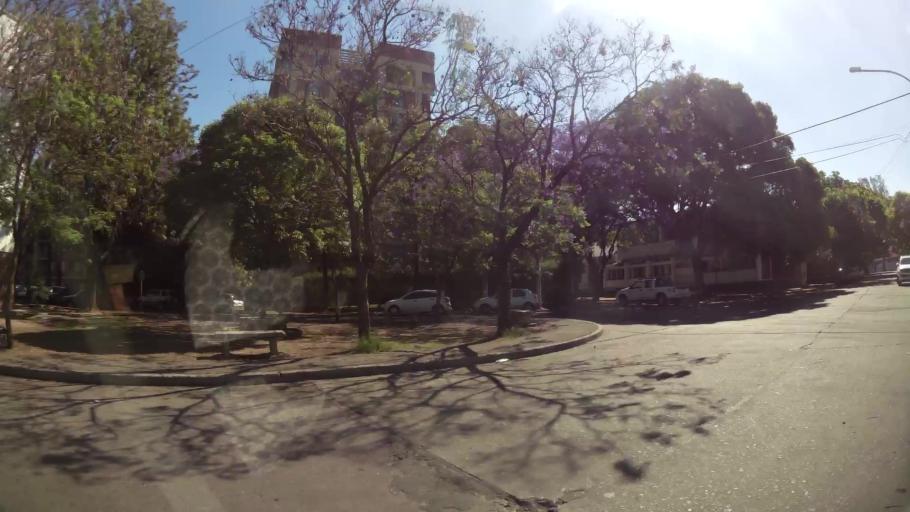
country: AR
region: Cordoba
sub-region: Departamento de Capital
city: Cordoba
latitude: -31.4207
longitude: -64.1698
